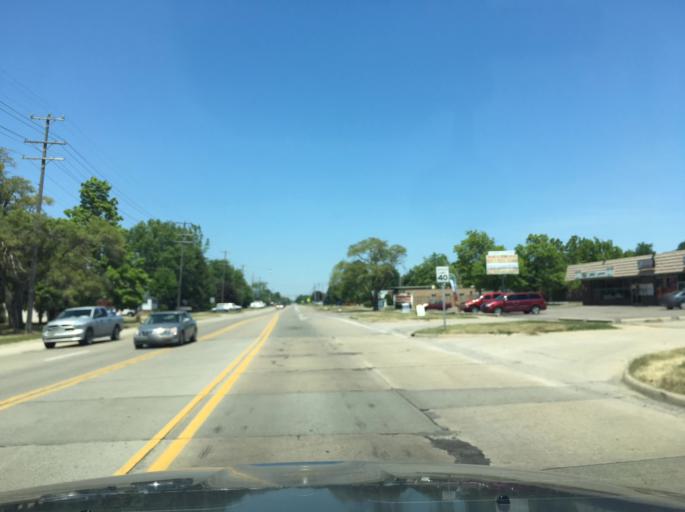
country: US
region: Michigan
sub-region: Macomb County
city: Fraser
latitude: 42.5397
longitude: -82.9497
